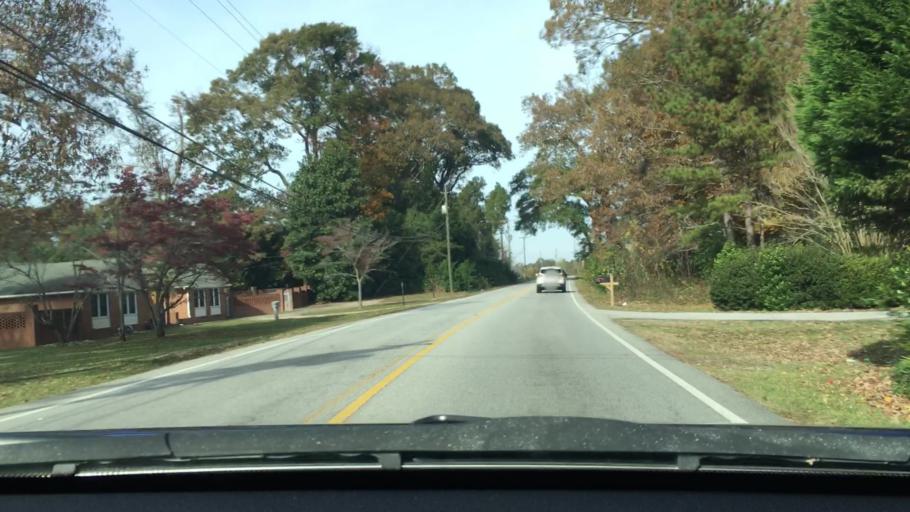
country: US
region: South Carolina
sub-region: Sumter County
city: South Sumter
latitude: 33.8985
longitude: -80.3699
